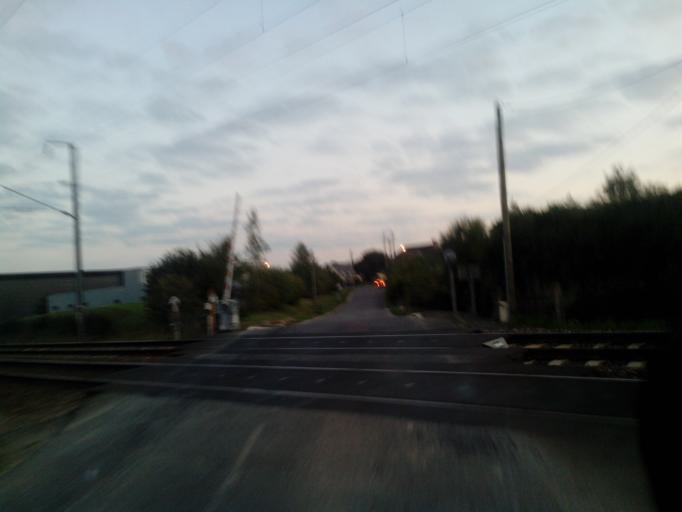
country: FR
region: Brittany
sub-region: Departement d'Ille-et-Vilaine
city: Montfort-sur-Meu
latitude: 48.1464
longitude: -1.9670
